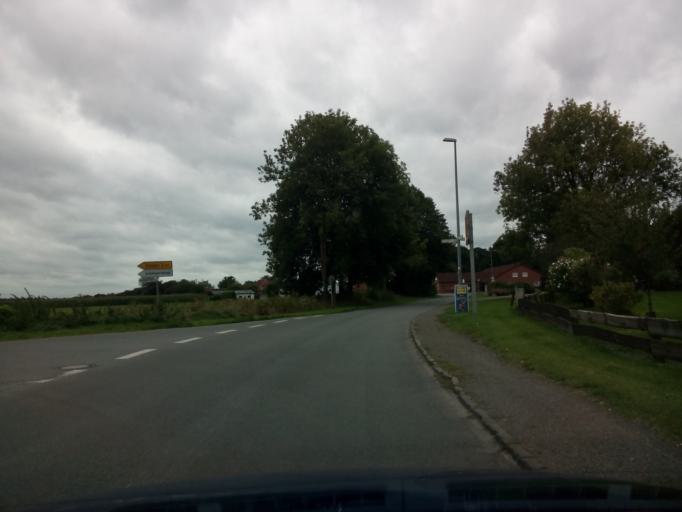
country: DE
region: Lower Saxony
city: Lubberstedt
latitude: 53.3694
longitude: 8.8266
